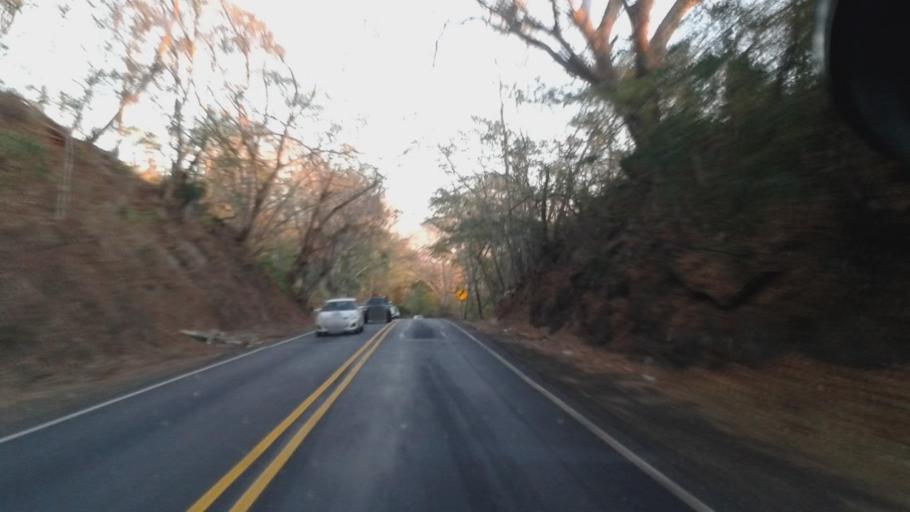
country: CR
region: Puntarenas
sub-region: Canton Central de Puntarenas
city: Puntarenas
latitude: 10.1260
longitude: -84.9003
